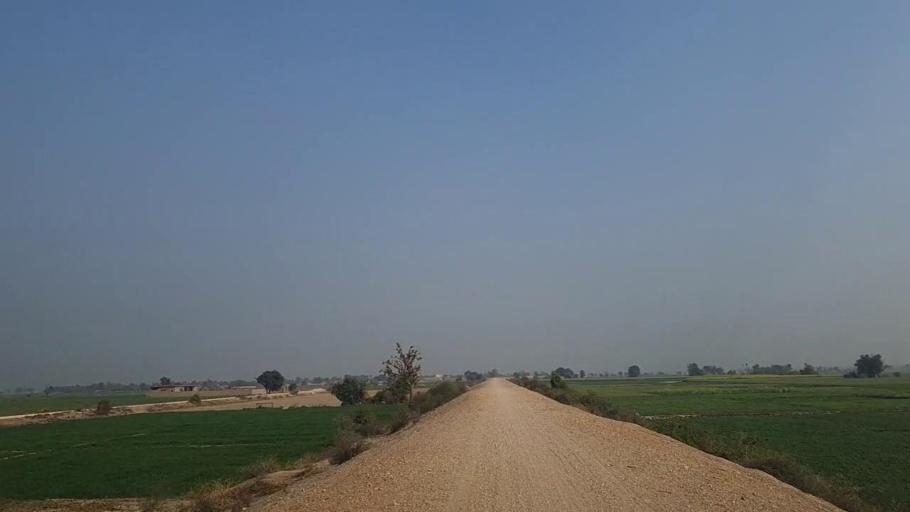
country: PK
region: Sindh
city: Sann
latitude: 26.0843
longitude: 68.1719
